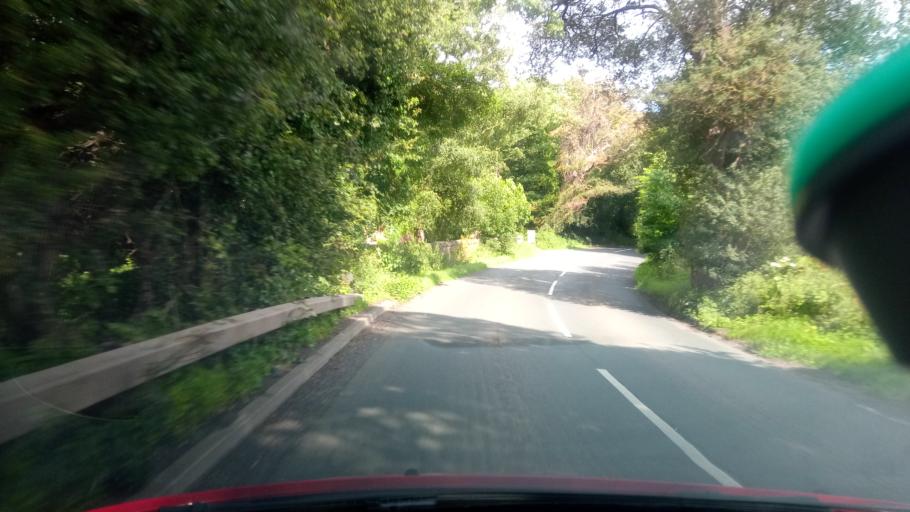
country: GB
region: Scotland
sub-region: East Lothian
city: Ormiston
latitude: 55.8963
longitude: -2.9469
